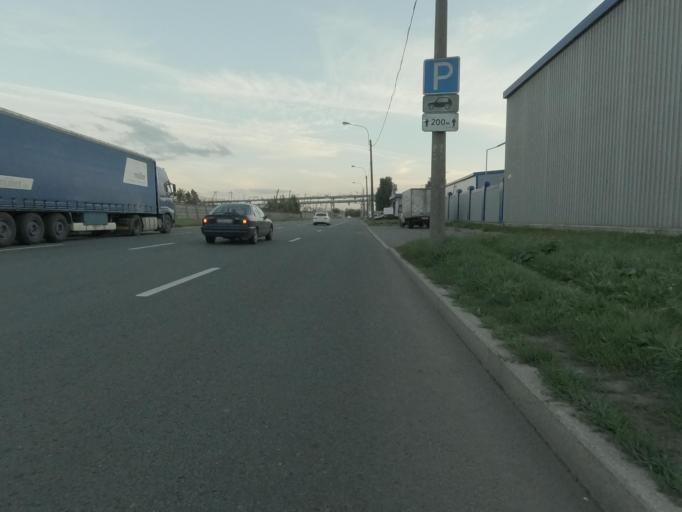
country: RU
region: St.-Petersburg
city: Vasyl'evsky Ostrov
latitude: 59.9064
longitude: 30.2364
